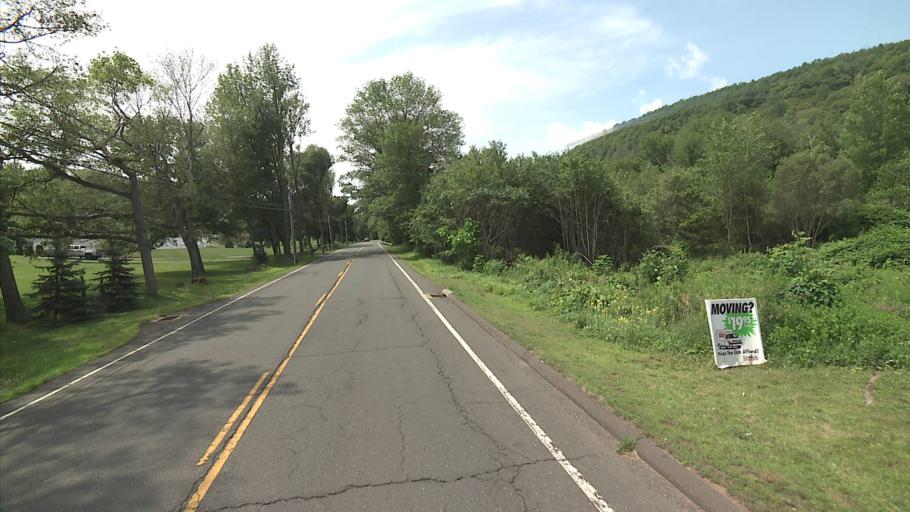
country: US
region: Connecticut
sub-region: Middlesex County
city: Durham
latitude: 41.4290
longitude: -72.7324
